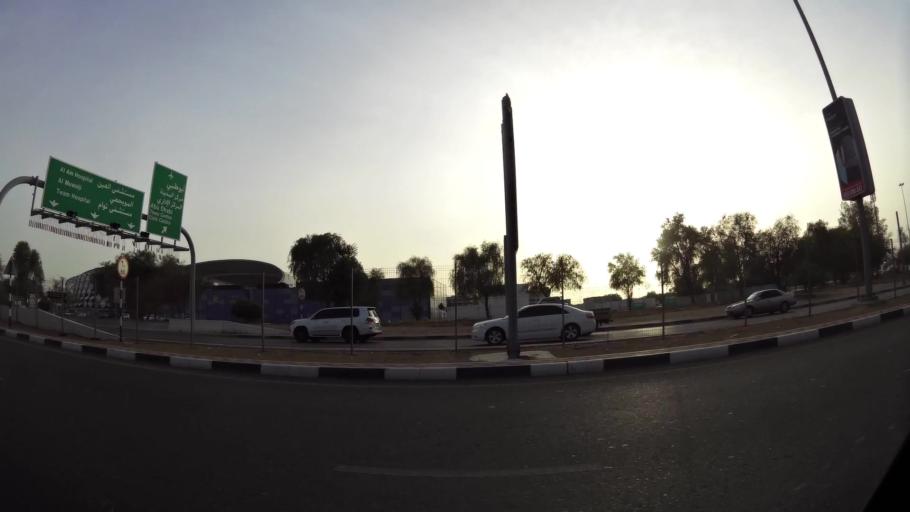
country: AE
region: Abu Dhabi
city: Al Ain
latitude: 24.2469
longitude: 55.7197
